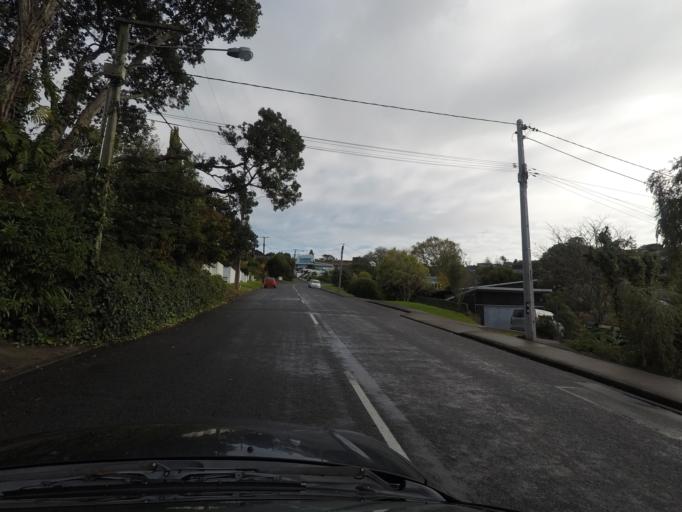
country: NZ
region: Auckland
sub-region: Auckland
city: Rothesay Bay
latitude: -36.7123
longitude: 174.7476
